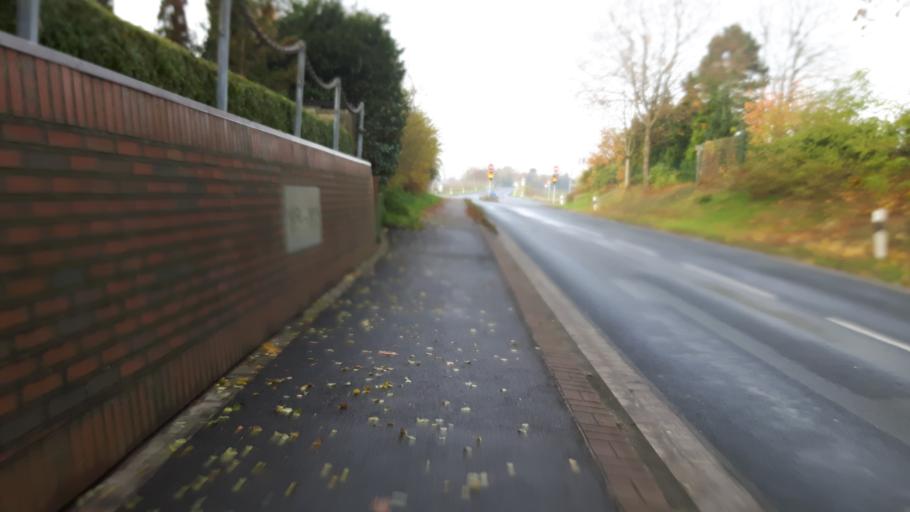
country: DE
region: Lower Saxony
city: Ganderkesee
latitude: 53.0181
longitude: 8.5721
